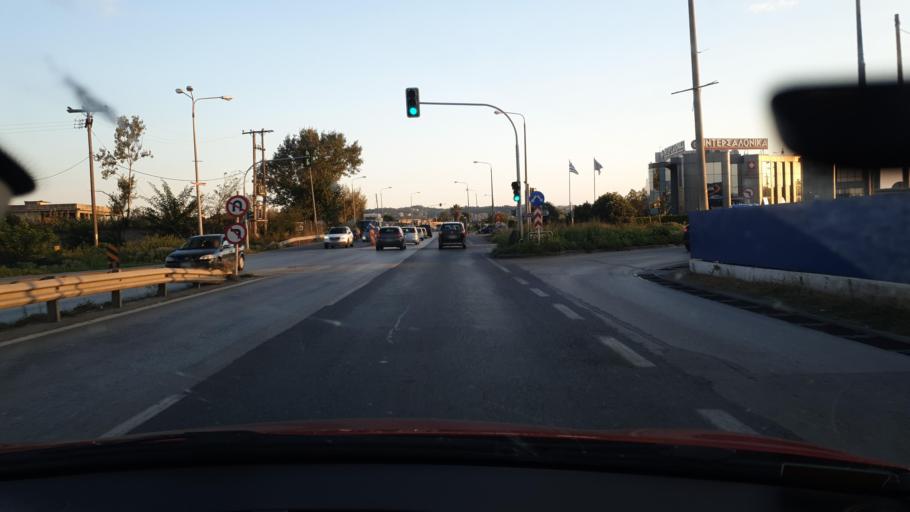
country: GR
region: Central Macedonia
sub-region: Nomos Thessalonikis
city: Neo Rysi
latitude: 40.5220
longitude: 22.9943
